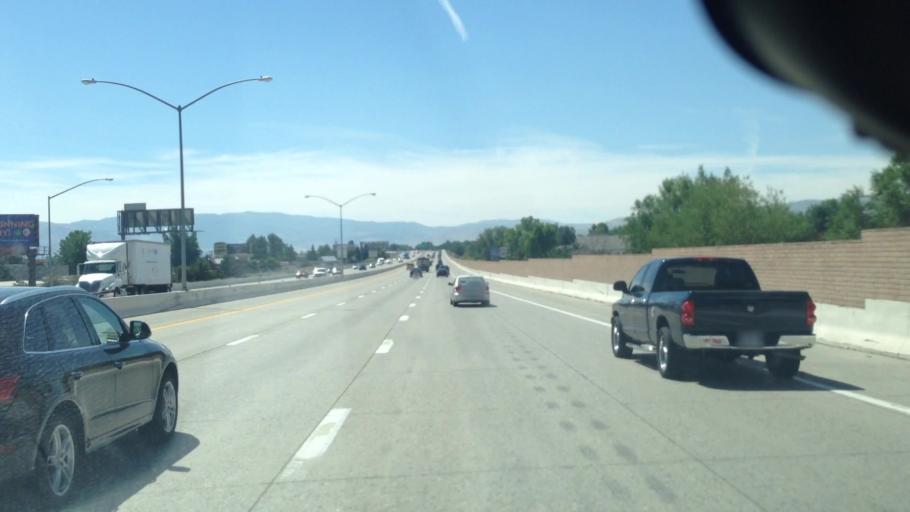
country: US
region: Nevada
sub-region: Washoe County
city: Reno
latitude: 39.4636
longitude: -119.7863
